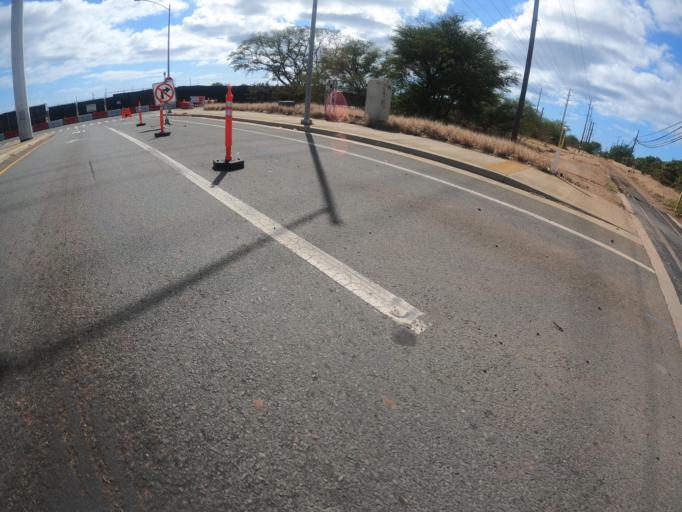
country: US
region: Hawaii
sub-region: Honolulu County
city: Makakilo City
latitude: 21.3256
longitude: -158.0867
